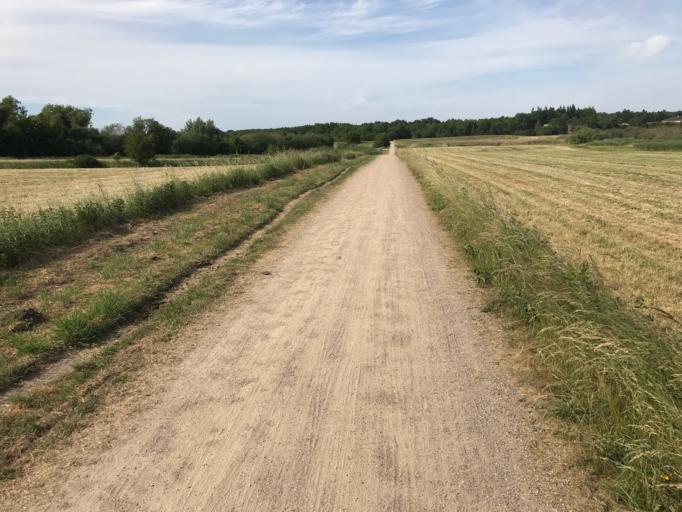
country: DK
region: Capital Region
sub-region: Fureso Kommune
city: Vaerlose
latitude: 55.7640
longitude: 12.3514
